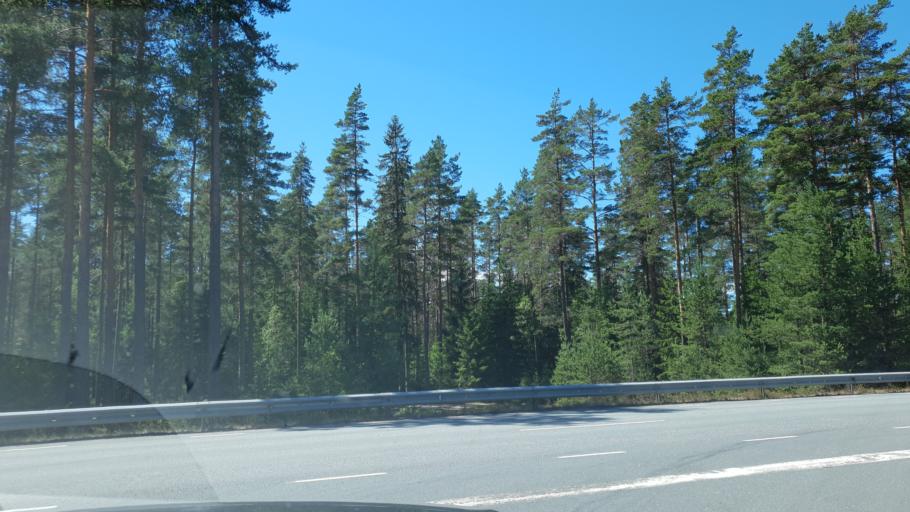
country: SE
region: Joenkoeping
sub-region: Vaggeryds Kommun
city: Vaggeryd
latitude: 57.5227
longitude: 14.1357
